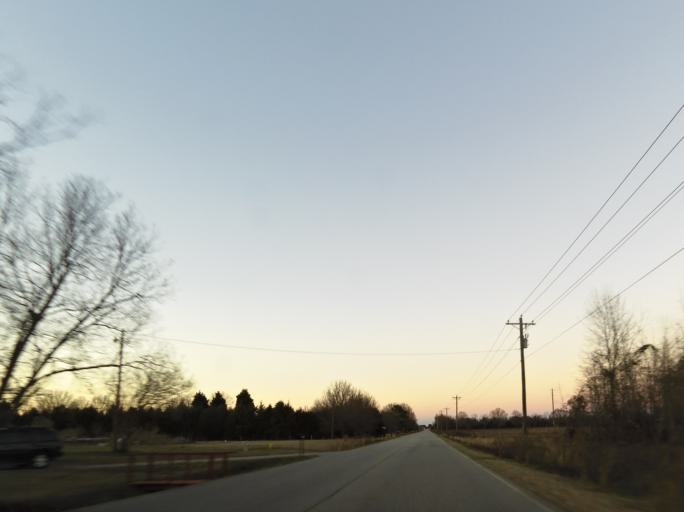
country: US
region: Georgia
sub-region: Peach County
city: Byron
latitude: 32.5992
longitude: -83.7481
